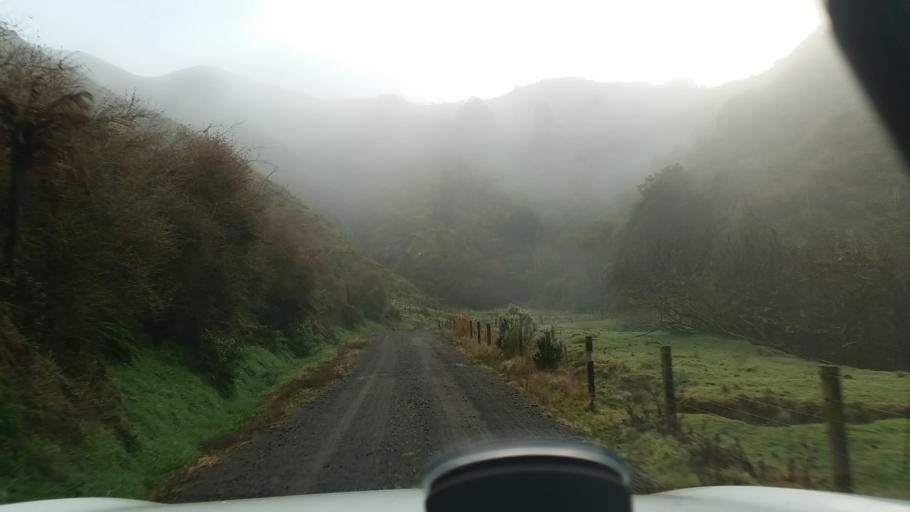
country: NZ
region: Taranaki
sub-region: South Taranaki District
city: Eltham
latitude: -39.4149
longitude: 174.4272
